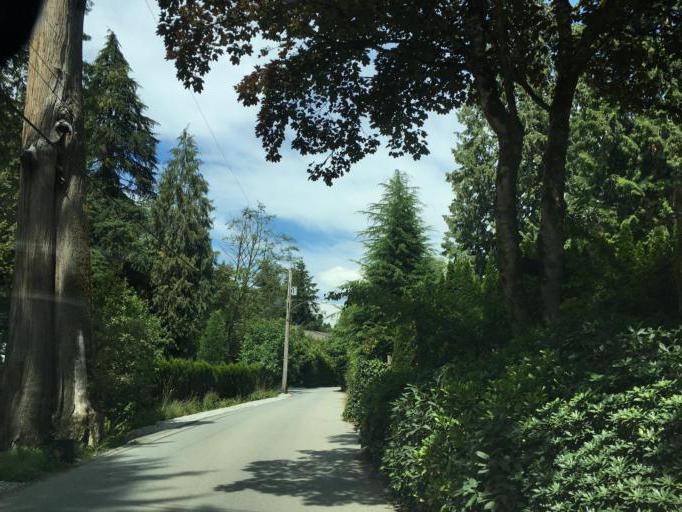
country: CA
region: British Columbia
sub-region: Greater Vancouver Regional District
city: Bowen Island
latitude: 49.3391
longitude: -123.2635
